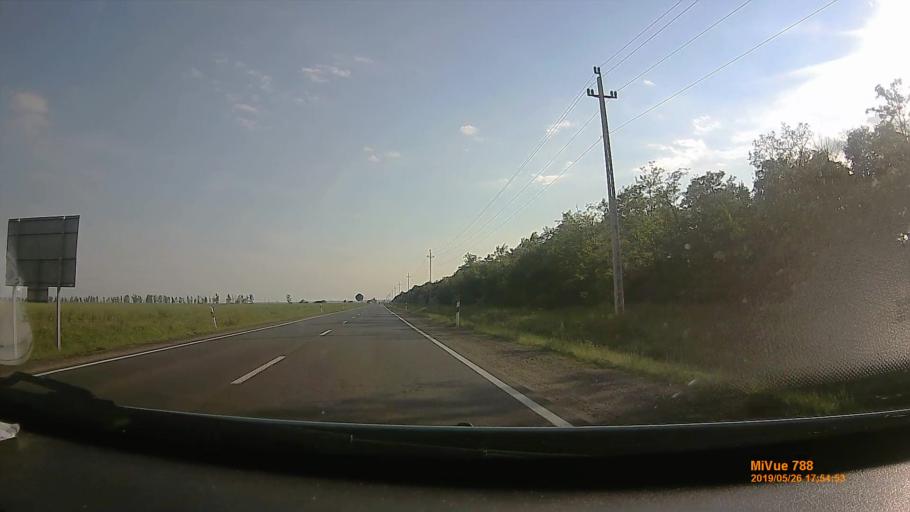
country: HU
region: Borsod-Abauj-Zemplen
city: Arnot
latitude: 48.1357
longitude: 20.8807
